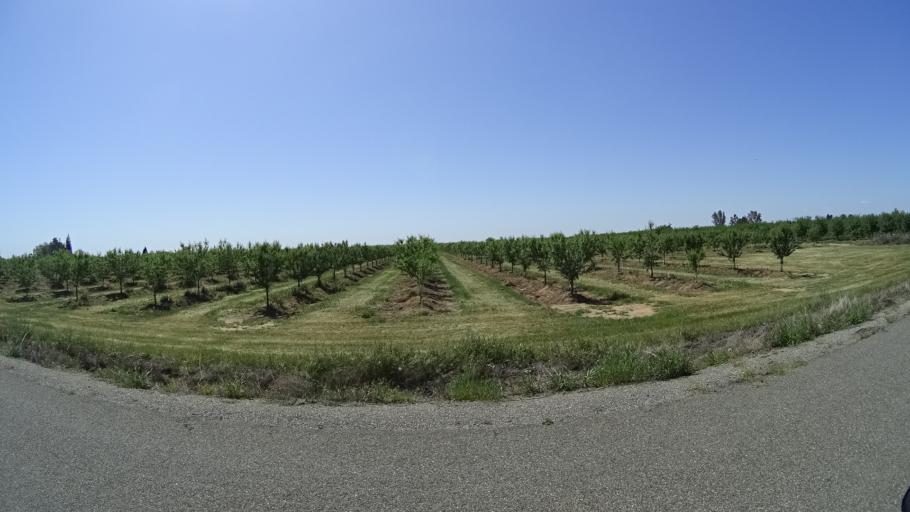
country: US
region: California
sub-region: Glenn County
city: Orland
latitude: 39.7871
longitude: -122.1729
